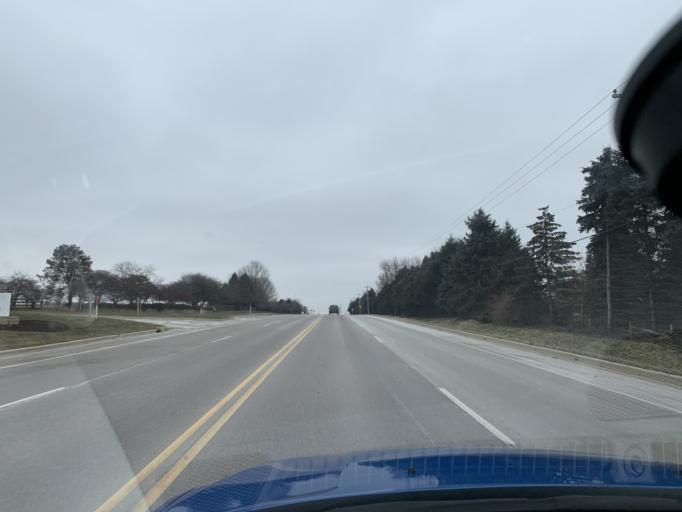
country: US
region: Wisconsin
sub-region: Dane County
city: Sun Prairie
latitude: 43.1922
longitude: -89.2643
